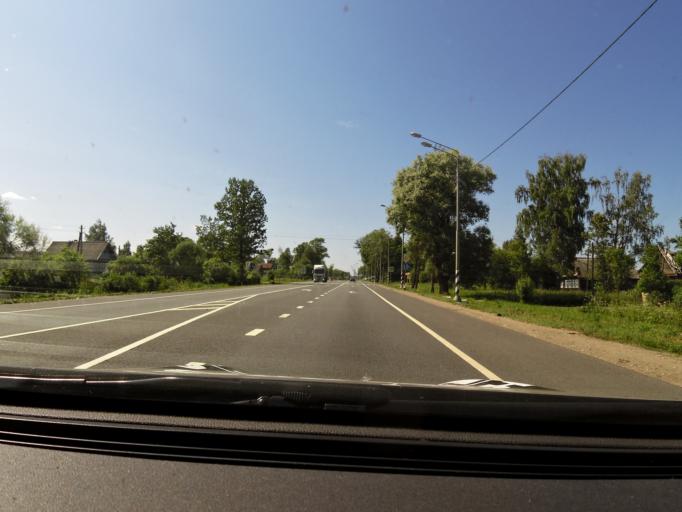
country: RU
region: Novgorod
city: Kresttsy
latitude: 58.3595
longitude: 32.2242
